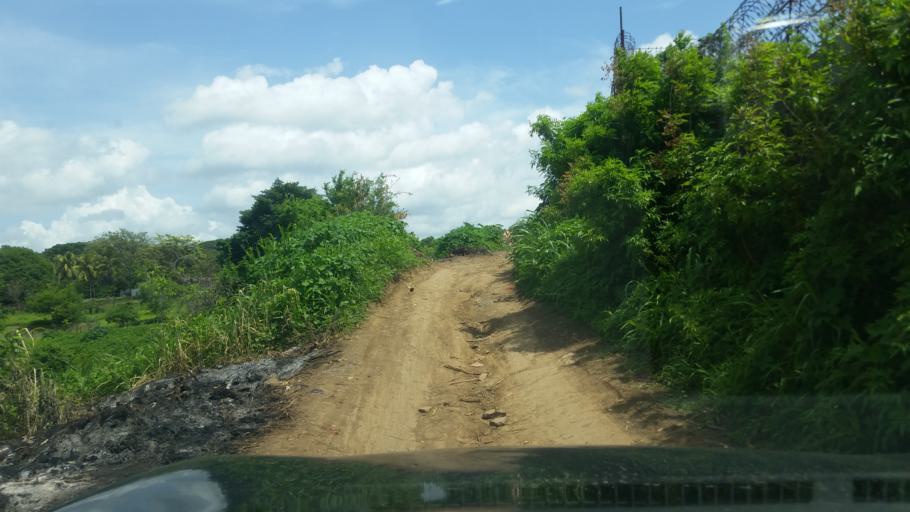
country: NI
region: Managua
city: Managua
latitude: 12.1024
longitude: -86.2402
